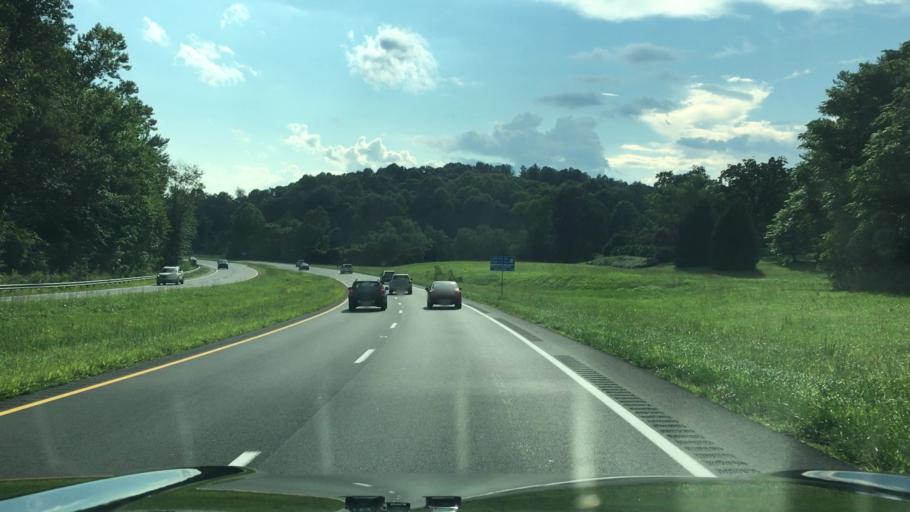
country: US
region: Virginia
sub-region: Albemarle County
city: Crozet
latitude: 37.9775
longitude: -78.6068
